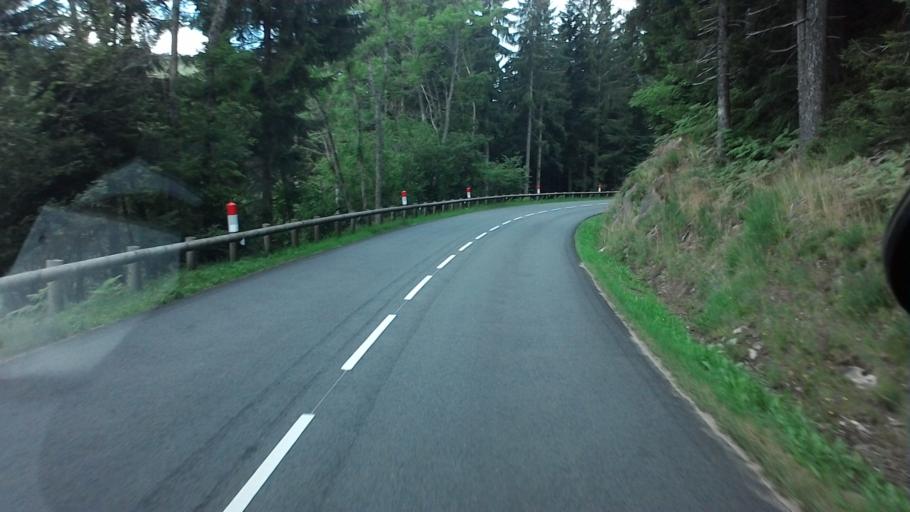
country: FR
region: Lorraine
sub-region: Departement des Vosges
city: Gerardmer
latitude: 48.0572
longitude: 6.8581
